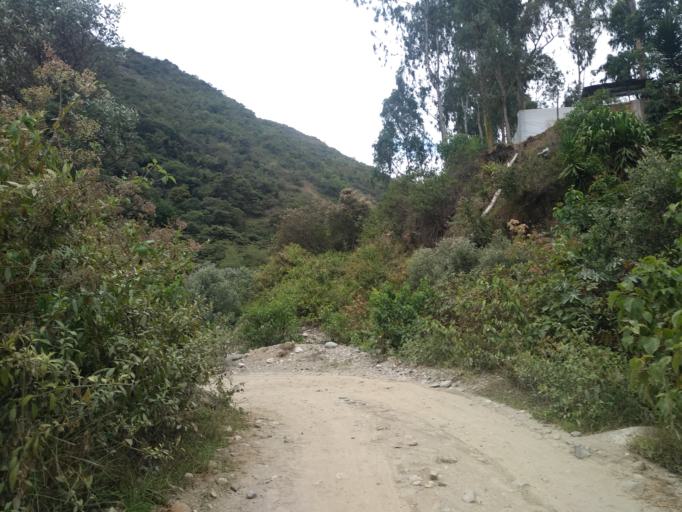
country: PE
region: Cusco
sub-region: Provincia de La Convencion
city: Santa Teresa
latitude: -13.2270
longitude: -72.6273
